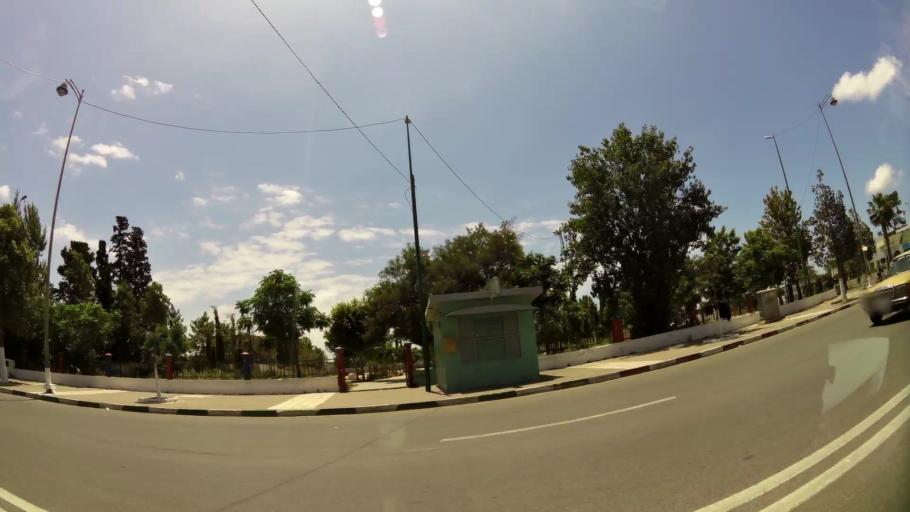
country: MA
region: Gharb-Chrarda-Beni Hssen
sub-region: Kenitra Province
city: Kenitra
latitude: 34.2530
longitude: -6.5586
